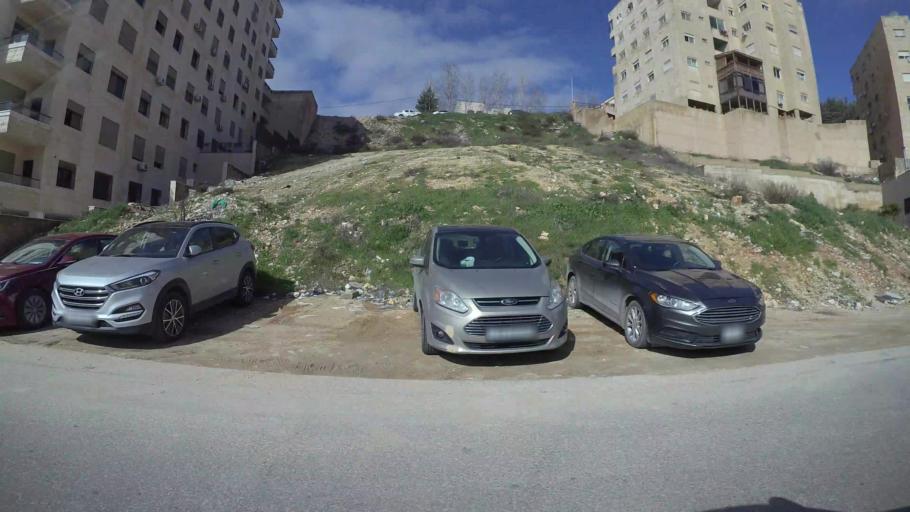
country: JO
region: Amman
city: Al Jubayhah
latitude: 32.0040
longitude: 35.8446
